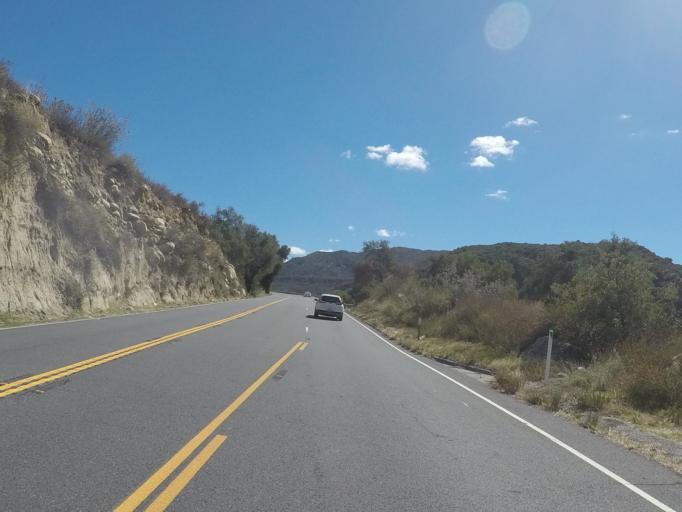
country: US
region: California
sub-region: Riverside County
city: Idyllwild-Pine Cove
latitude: 33.7227
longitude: -116.8019
